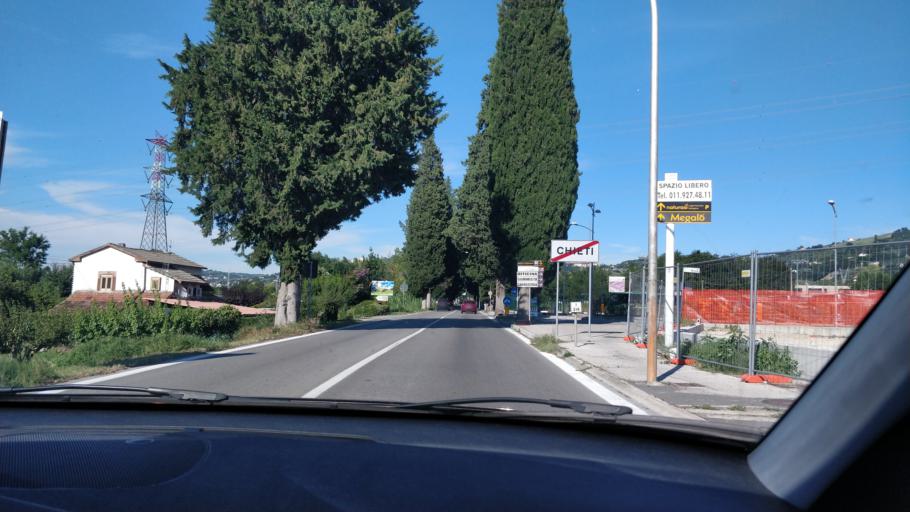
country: IT
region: Abruzzo
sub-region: Provincia di Chieti
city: Casalincontrada
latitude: 42.3322
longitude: 14.1185
